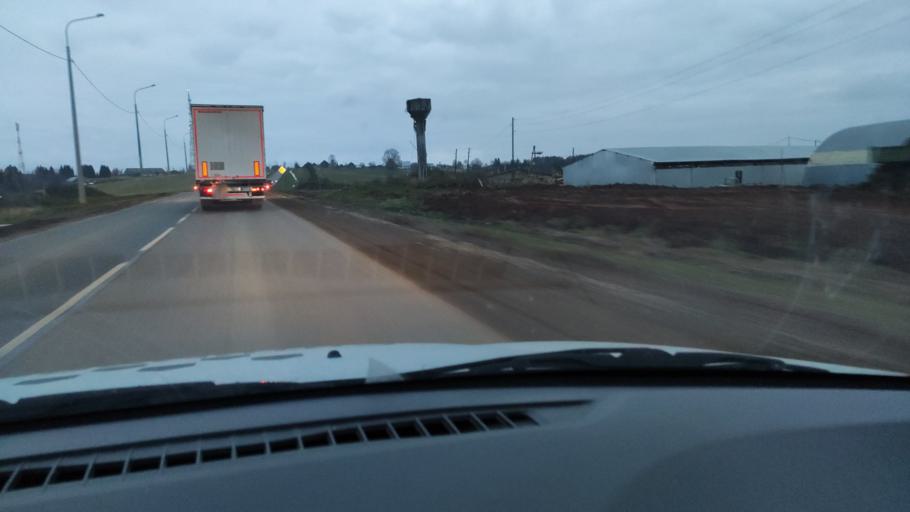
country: RU
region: Kirov
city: Kostino
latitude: 58.8510
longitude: 53.2731
